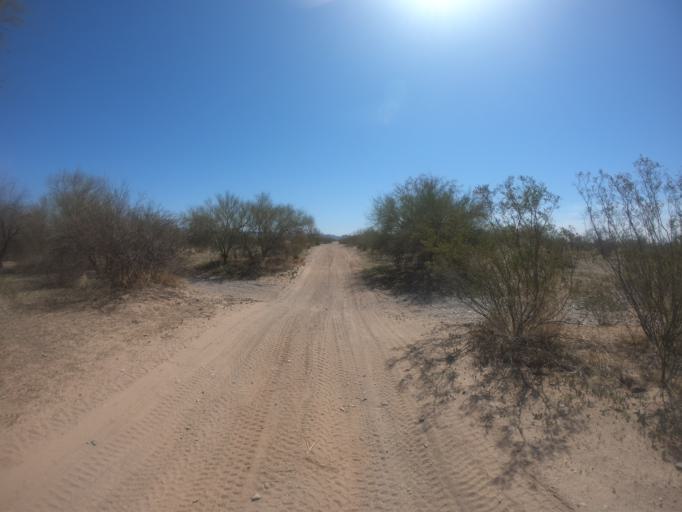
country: US
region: Arizona
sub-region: Pinal County
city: Gold Camp
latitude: 33.2409
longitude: -111.3157
